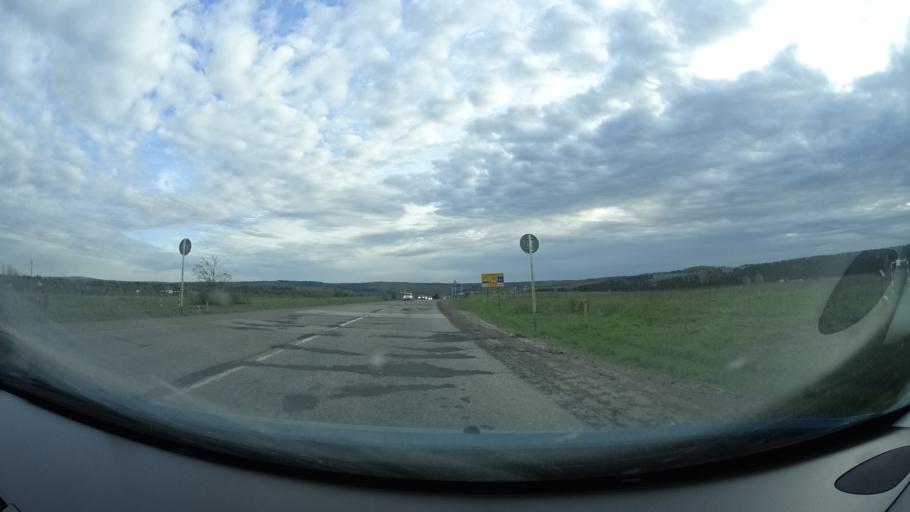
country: RU
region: Perm
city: Yugo-Kamskiy
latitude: 57.4699
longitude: 55.6760
